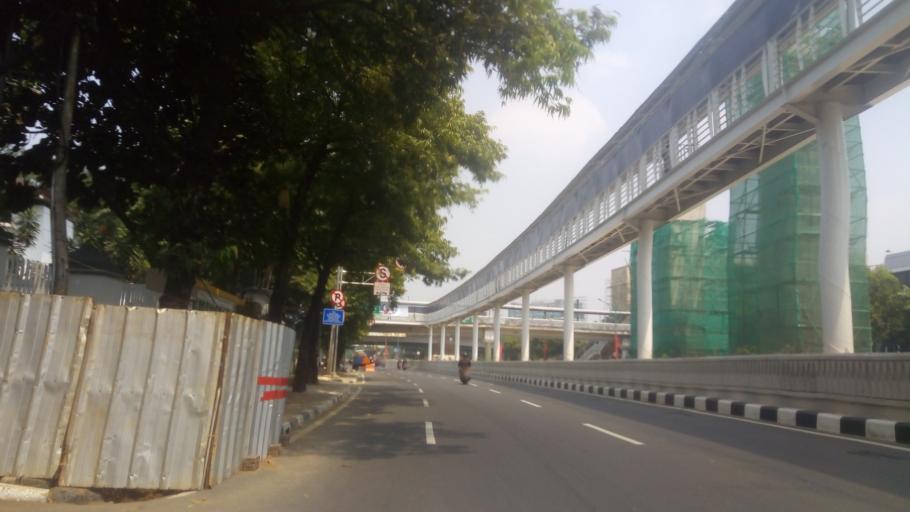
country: ID
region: Jakarta Raya
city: Jakarta
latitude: -6.2354
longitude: 106.8287
